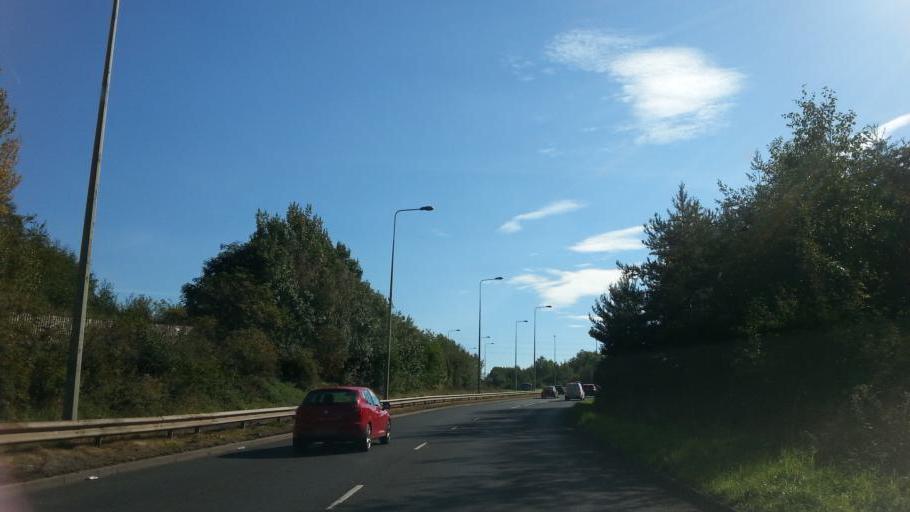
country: GB
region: England
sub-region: Shropshire
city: Hadley
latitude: 52.6943
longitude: -2.4905
